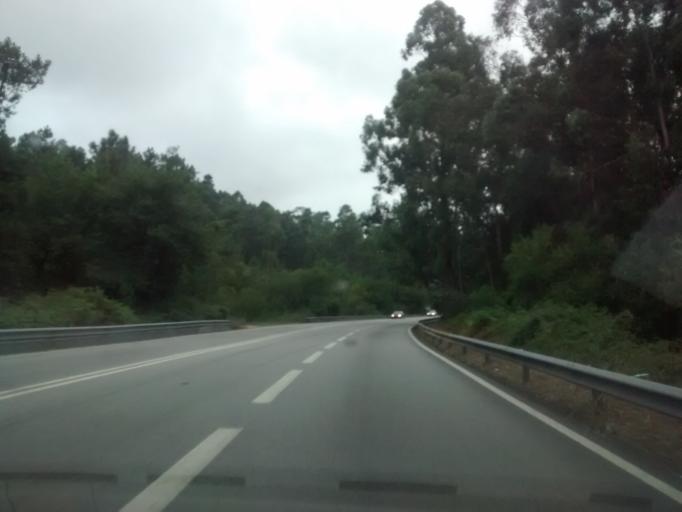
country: PT
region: Braga
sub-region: Braga
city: Oliveira
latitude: 41.4996
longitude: -8.4566
